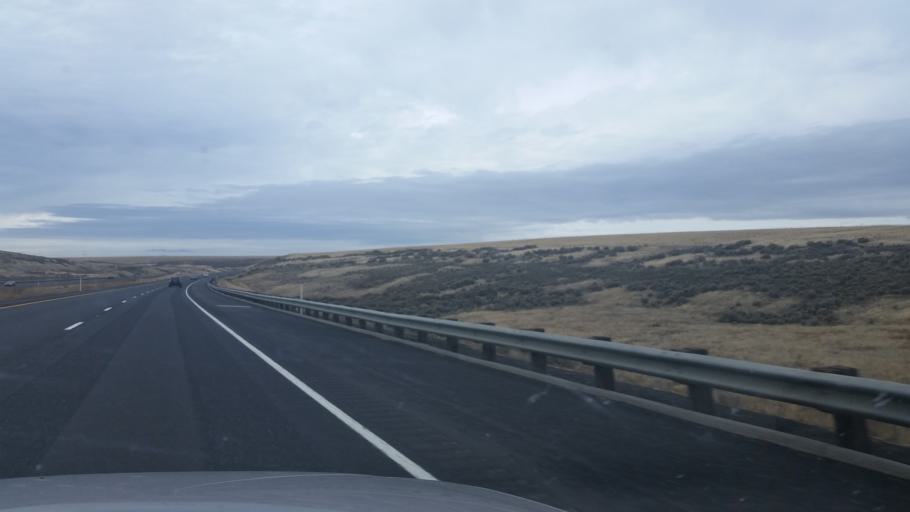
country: US
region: Washington
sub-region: Adams County
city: Ritzville
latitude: 47.1109
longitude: -118.5517
